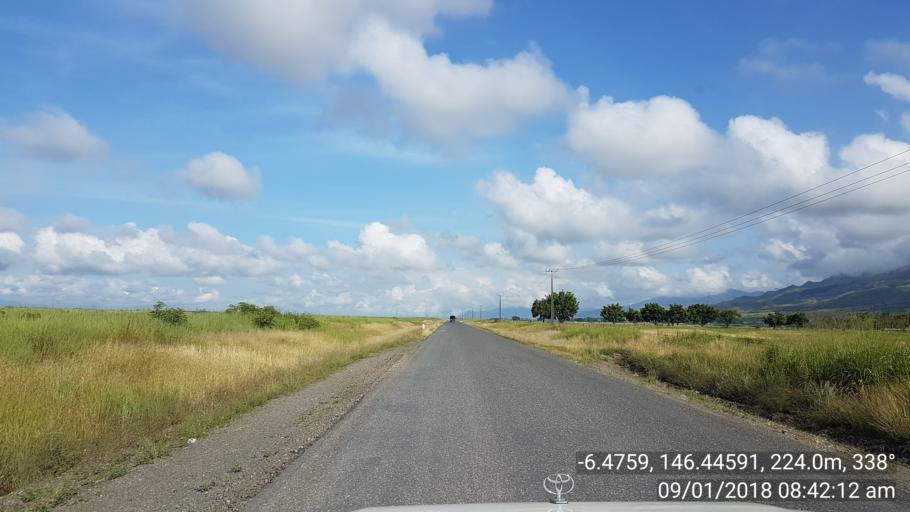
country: PG
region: Morobe
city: Lae
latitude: -6.4761
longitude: 146.4462
